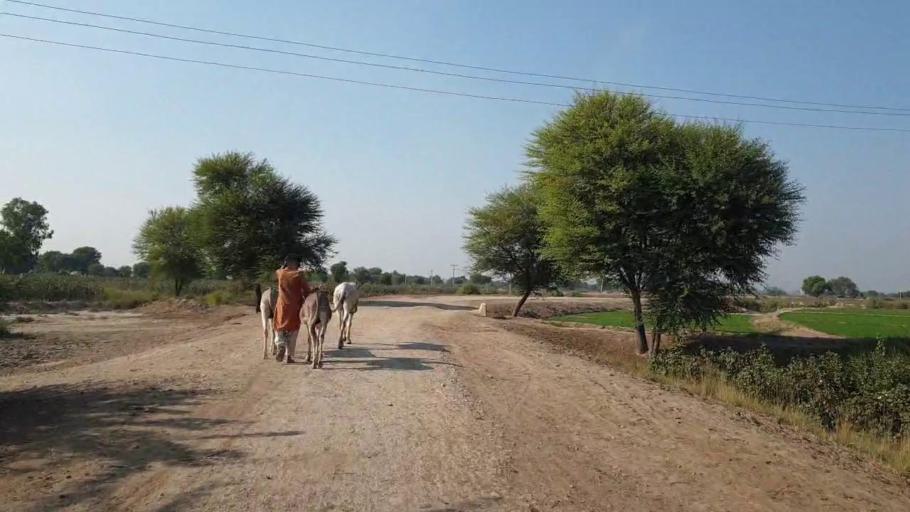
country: PK
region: Sindh
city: Sehwan
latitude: 26.4513
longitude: 67.8167
